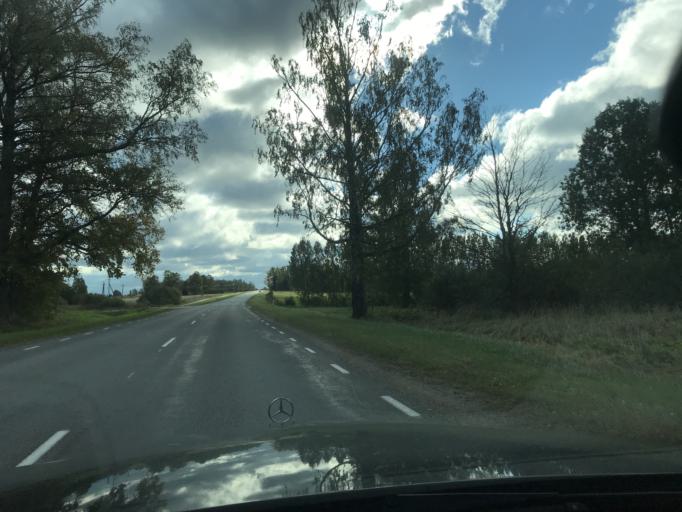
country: EE
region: Vorumaa
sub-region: Antsla vald
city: Vana-Antsla
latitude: 57.9402
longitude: 26.3082
